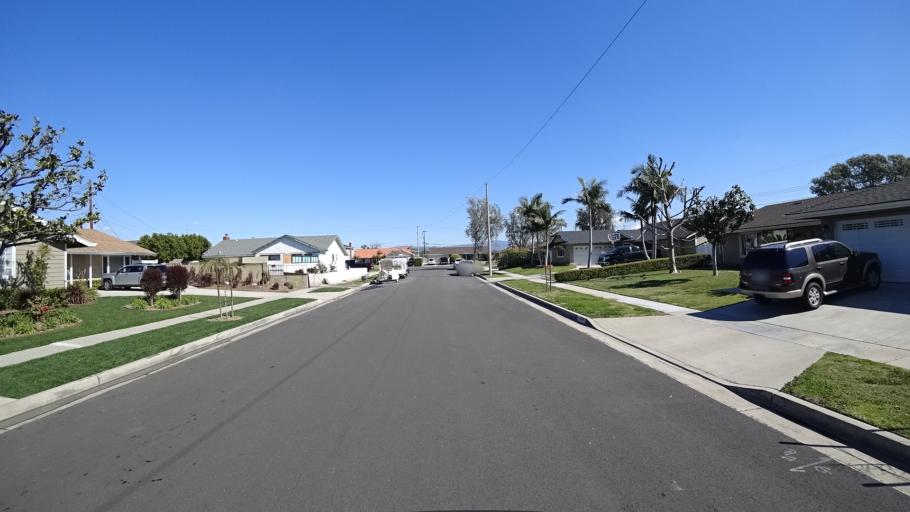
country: US
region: California
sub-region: Orange County
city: Placentia
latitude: 33.8308
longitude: -117.8709
